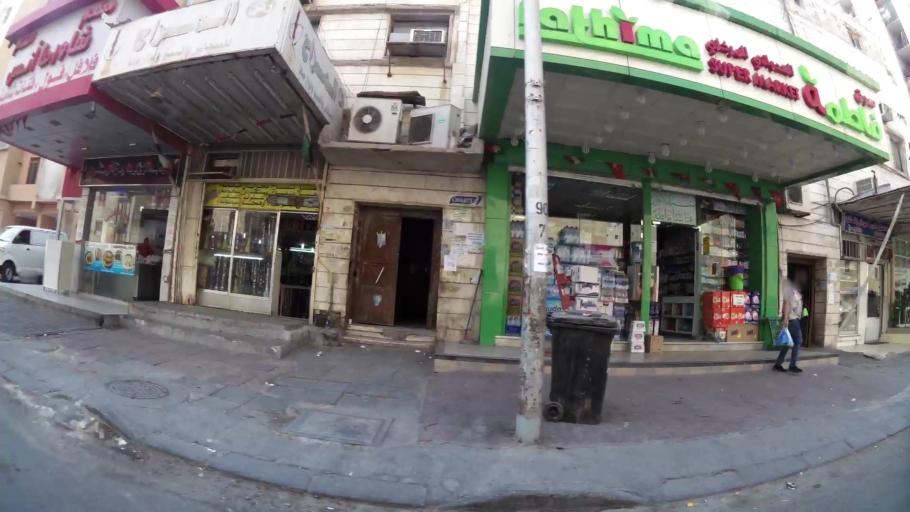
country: KW
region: Al Farwaniyah
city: Al Farwaniyah
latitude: 29.2782
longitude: 47.9586
